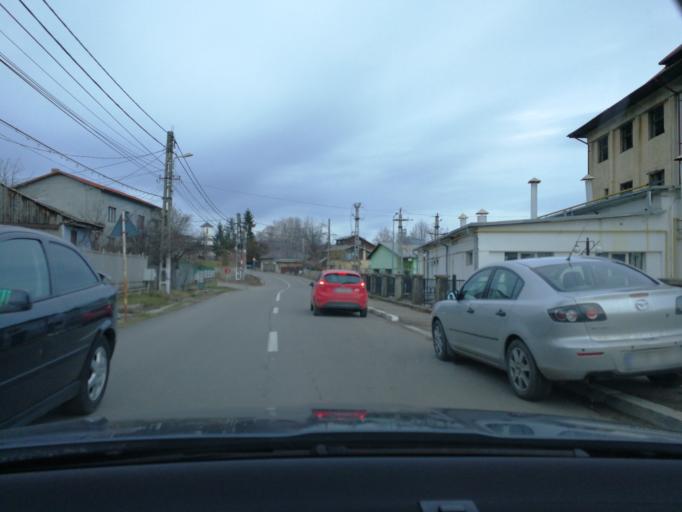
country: RO
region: Prahova
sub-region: Comuna Poiana Campina
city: Poiana Campina
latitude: 45.1296
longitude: 25.7079
